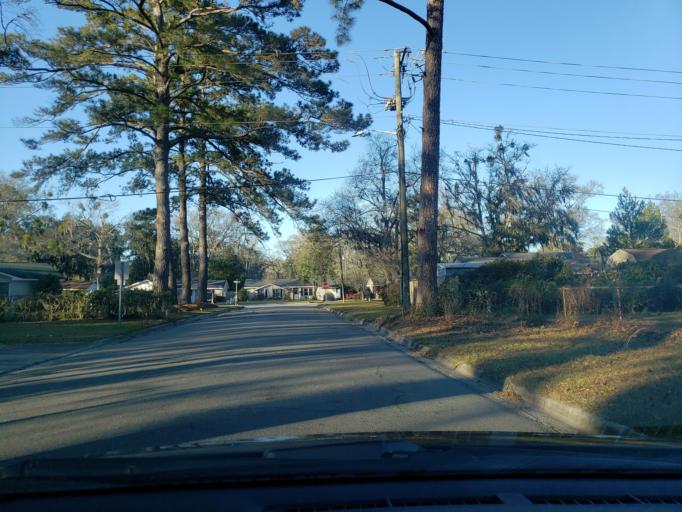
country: US
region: Georgia
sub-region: Chatham County
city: Montgomery
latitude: 31.9860
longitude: -81.1439
